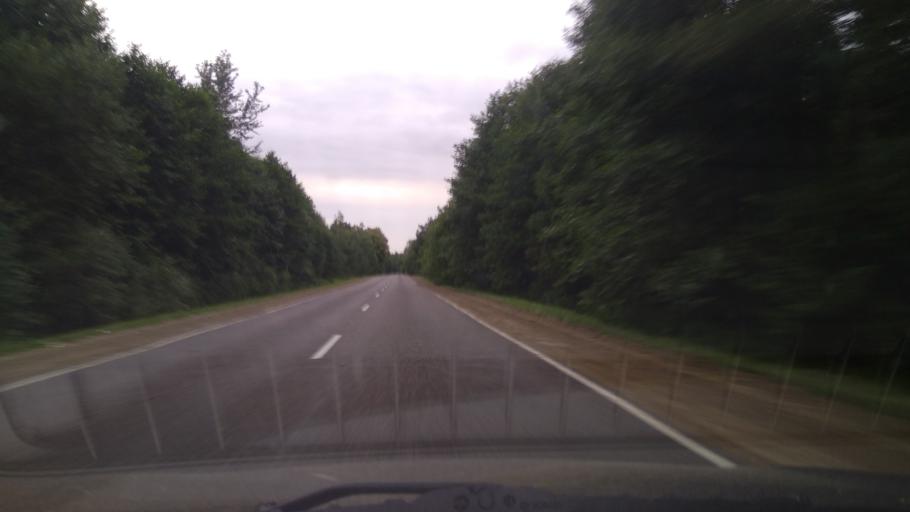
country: BY
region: Brest
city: Byaroza
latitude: 52.4099
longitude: 24.9944
